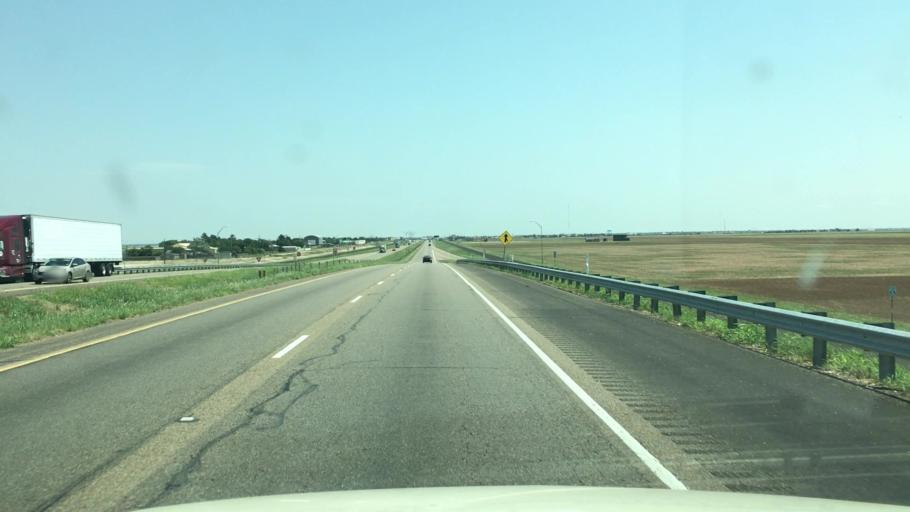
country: US
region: Texas
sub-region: Potter County
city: Bushland
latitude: 35.1899
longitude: -102.0094
